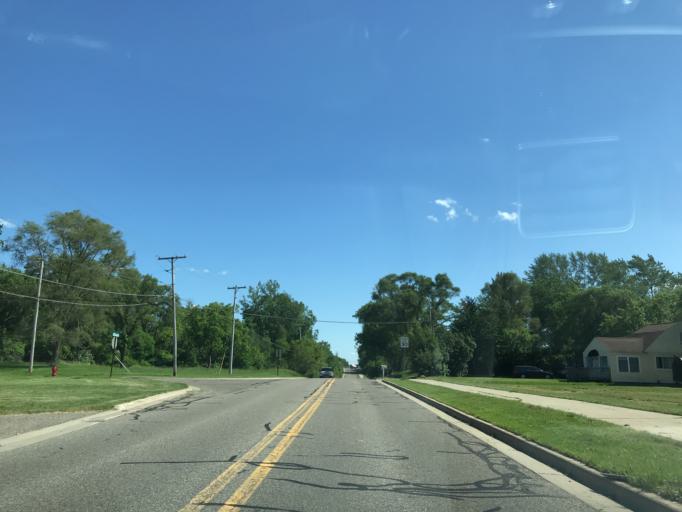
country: US
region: Michigan
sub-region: Oakland County
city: Novi
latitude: 42.5088
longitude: -83.4768
